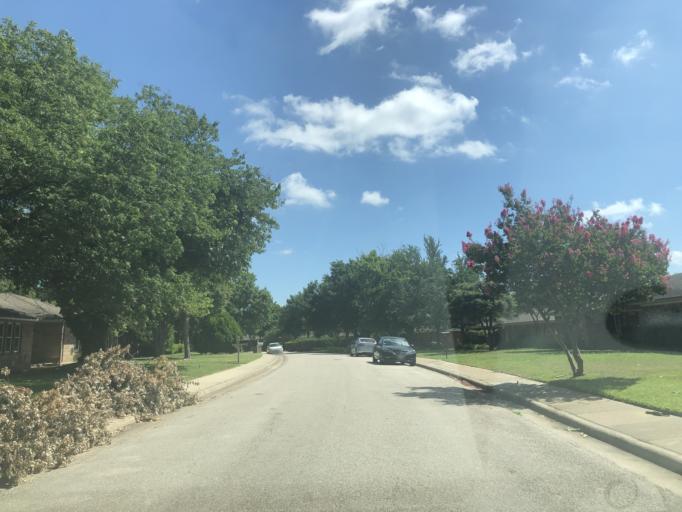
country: US
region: Texas
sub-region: Dallas County
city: Duncanville
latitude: 32.6528
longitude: -96.9272
